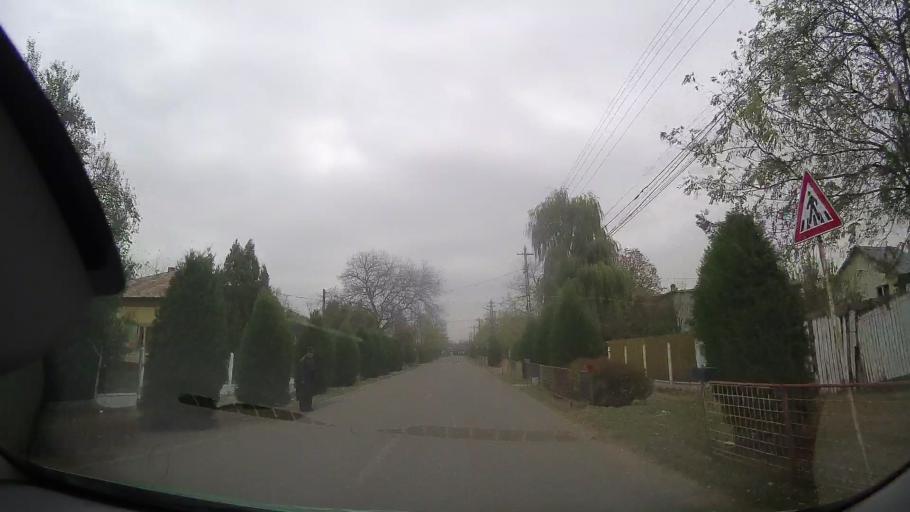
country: RO
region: Buzau
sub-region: Comuna Bradeanu
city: Bradeanu
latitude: 44.9236
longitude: 26.8650
